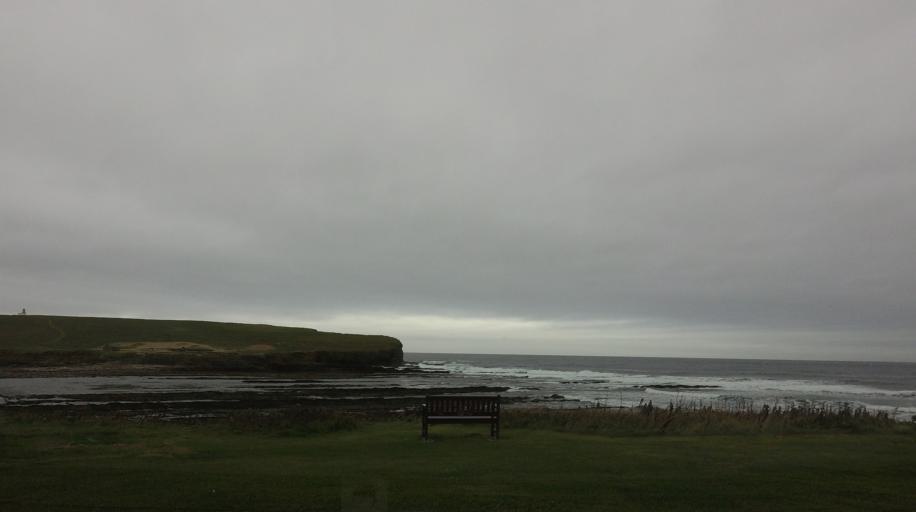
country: GB
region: Scotland
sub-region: Orkney Islands
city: Stromness
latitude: 59.1354
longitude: -3.3249
